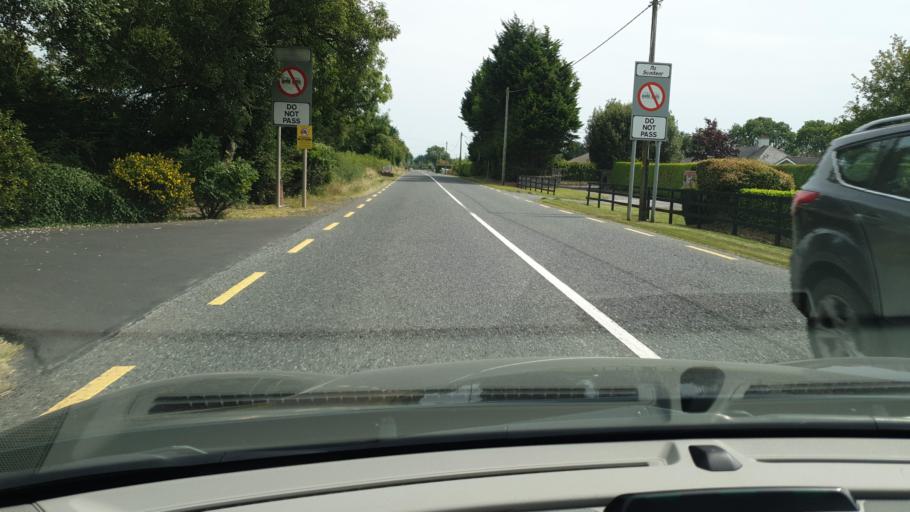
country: IE
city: Kentstown
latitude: 53.6296
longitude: -6.5446
